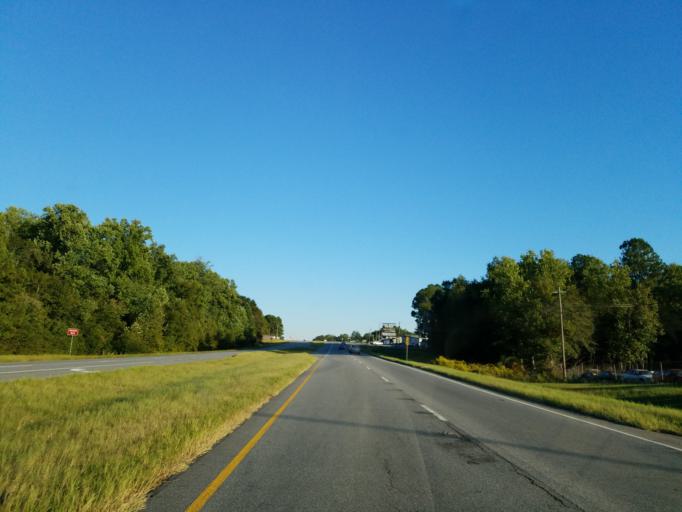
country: US
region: Georgia
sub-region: Worth County
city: Sylvester
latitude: 31.5214
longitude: -83.7891
